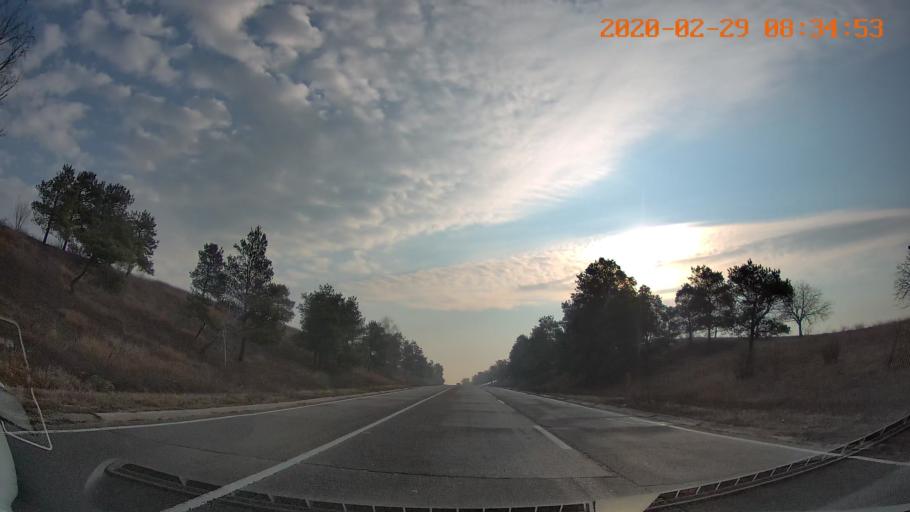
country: MD
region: Anenii Noi
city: Anenii Noi
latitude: 46.9236
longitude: 29.3174
